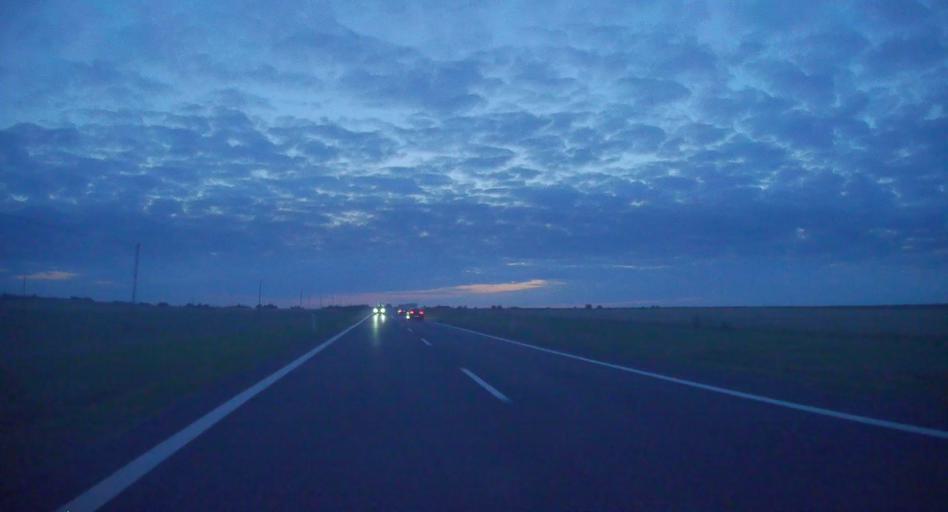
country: PL
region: Silesian Voivodeship
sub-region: Powiat klobucki
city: Klobuck
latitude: 50.8903
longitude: 18.9673
